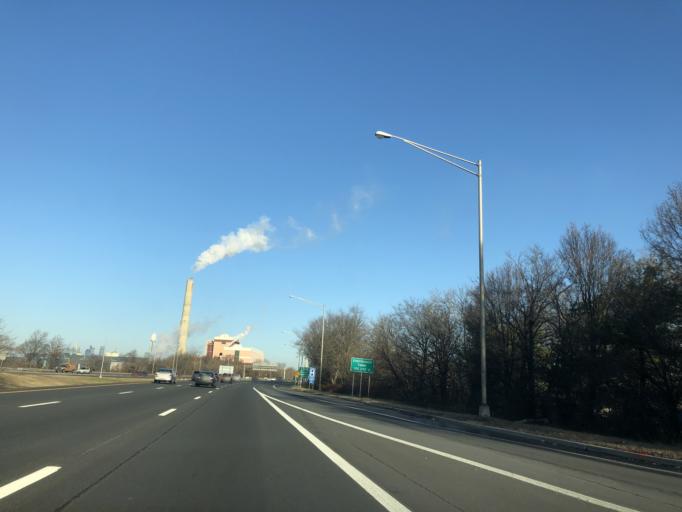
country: US
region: New Jersey
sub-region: Camden County
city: Gloucester City
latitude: 39.9042
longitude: -75.1124
